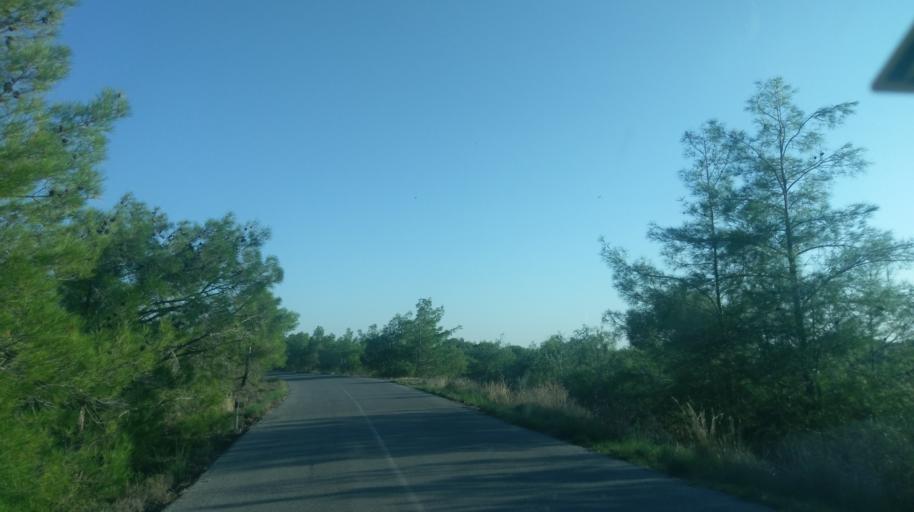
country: CY
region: Ammochostos
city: Lefkonoiko
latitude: 35.2898
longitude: 33.6521
